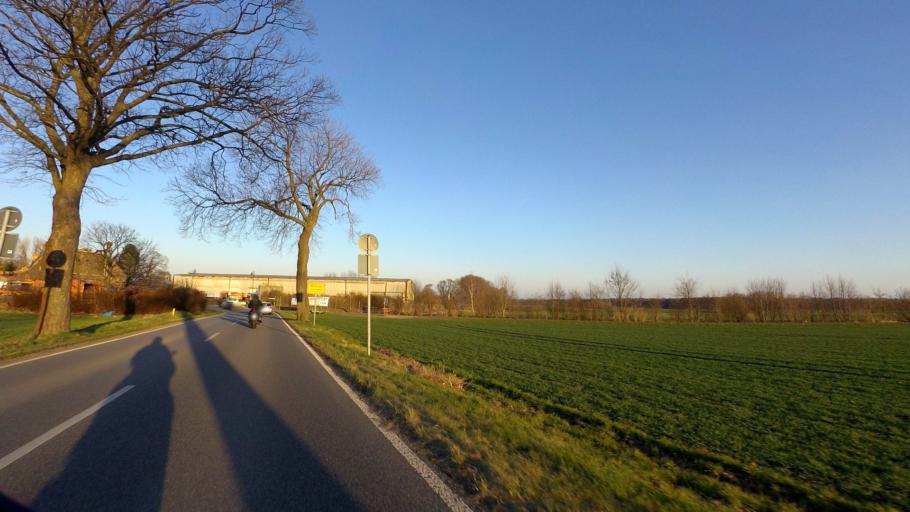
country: DE
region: Brandenburg
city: Ahrensfelde
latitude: 52.5705
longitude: 13.6128
